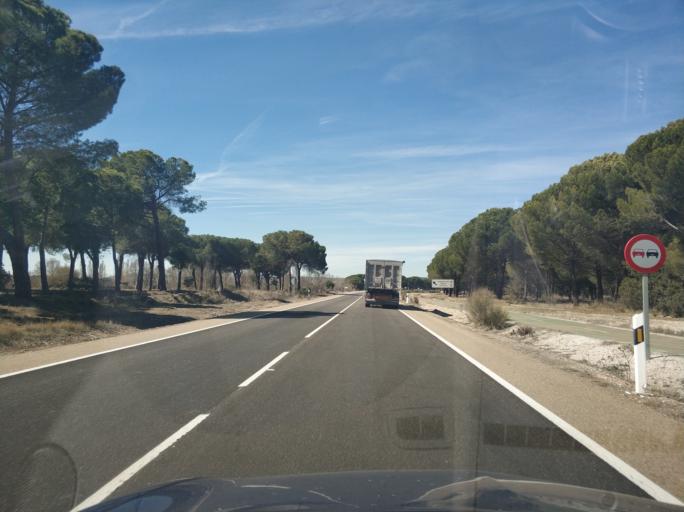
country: ES
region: Castille and Leon
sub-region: Provincia de Valladolid
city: Simancas
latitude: 41.5648
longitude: -4.7962
